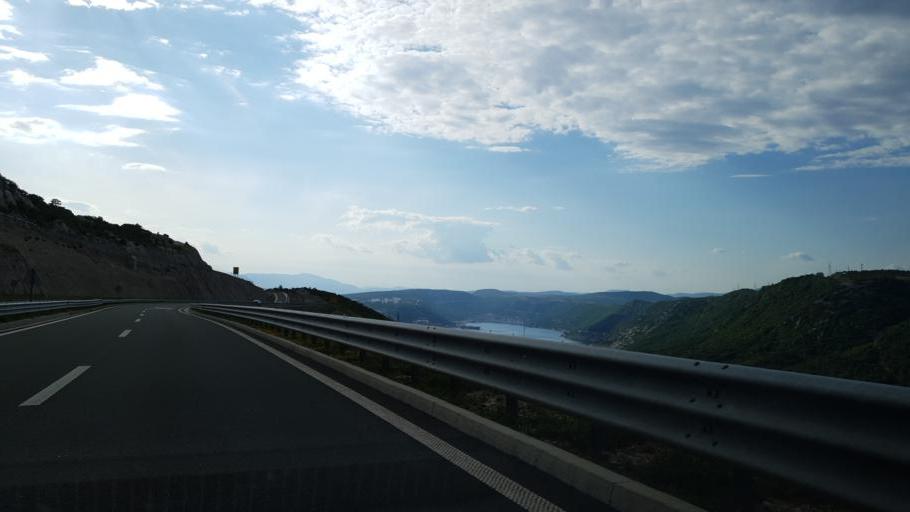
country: HR
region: Primorsko-Goranska
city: Hreljin
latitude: 45.2664
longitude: 14.6008
